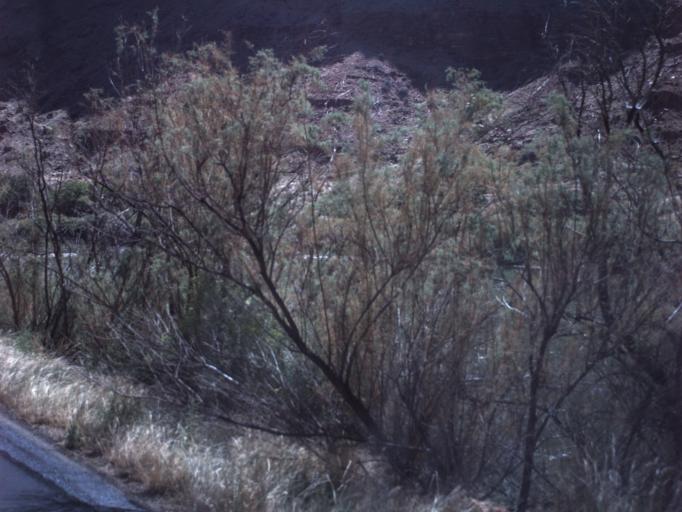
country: US
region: Utah
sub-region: Grand County
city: Moab
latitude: 38.6462
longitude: -109.5040
